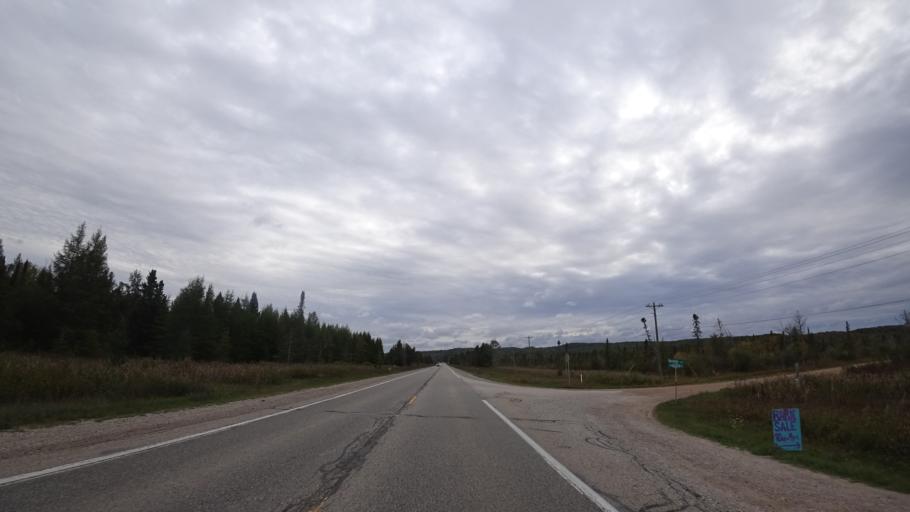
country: US
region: Michigan
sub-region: Charlevoix County
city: Boyne City
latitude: 45.2261
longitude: -84.9197
